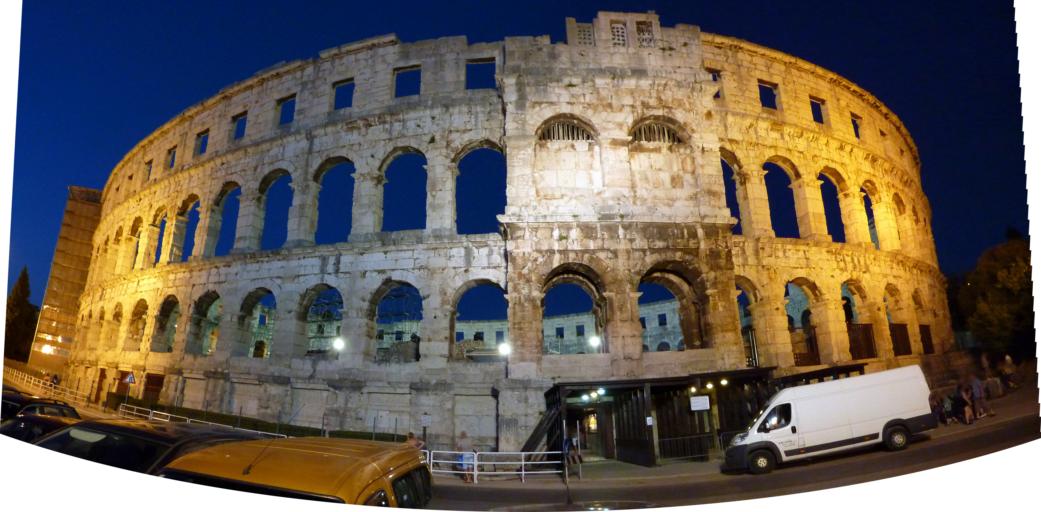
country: HR
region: Istarska
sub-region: Grad Pula
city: Pula
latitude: 44.8731
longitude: 13.8493
